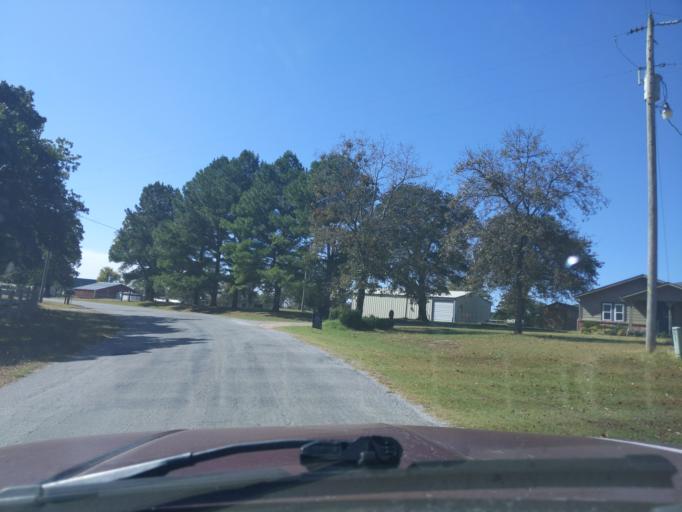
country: US
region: Oklahoma
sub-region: Creek County
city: Bristow
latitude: 35.7046
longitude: -96.4092
